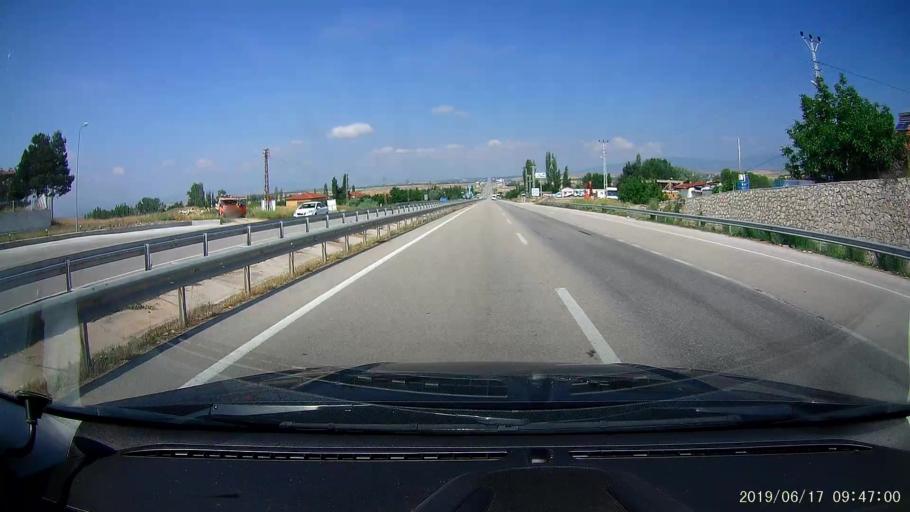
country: TR
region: Amasya
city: Suluova
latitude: 40.8774
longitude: 35.5890
